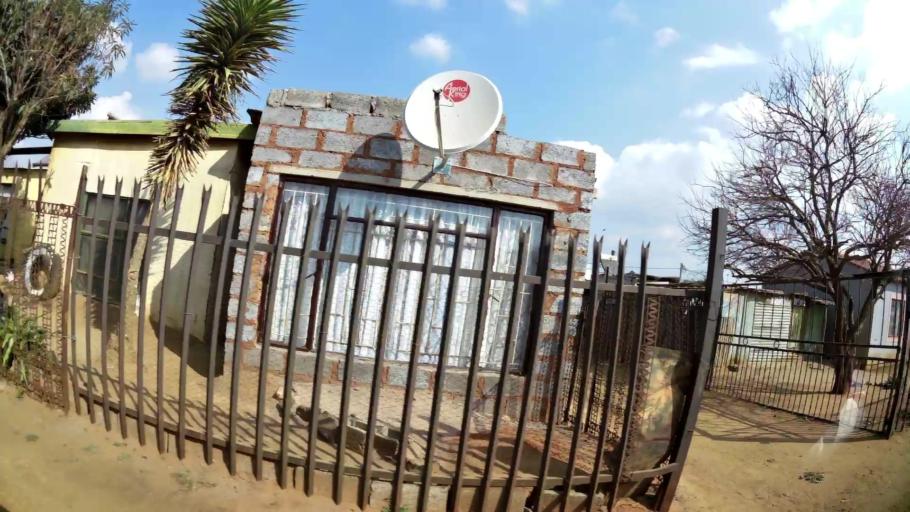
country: ZA
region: Gauteng
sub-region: Ekurhuleni Metropolitan Municipality
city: Springs
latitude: -26.1248
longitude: 28.4792
